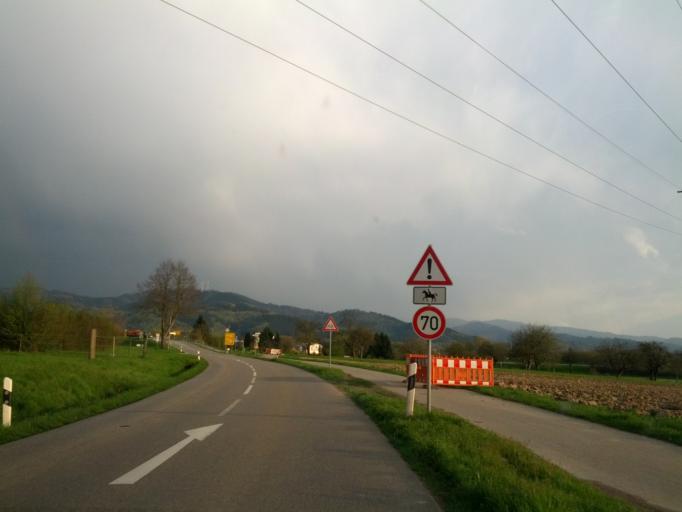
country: DE
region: Baden-Wuerttemberg
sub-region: Freiburg Region
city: Vorstetten
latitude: 48.0533
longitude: 7.8555
